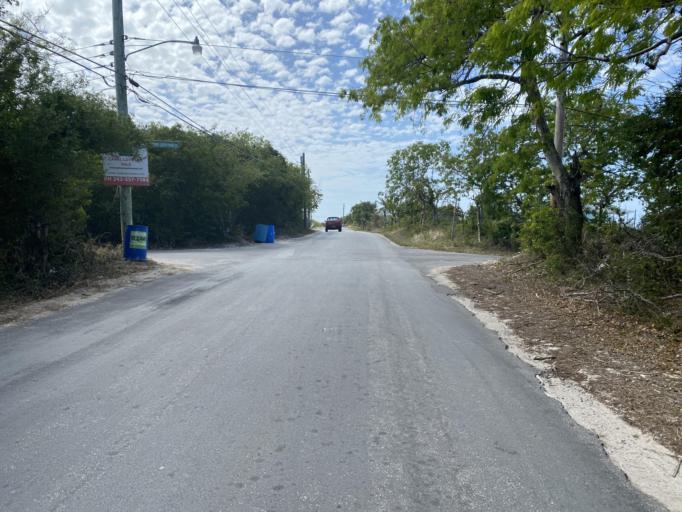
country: BS
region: Spanish Wells
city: Spanish Wells
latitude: 25.5440
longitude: -76.7841
